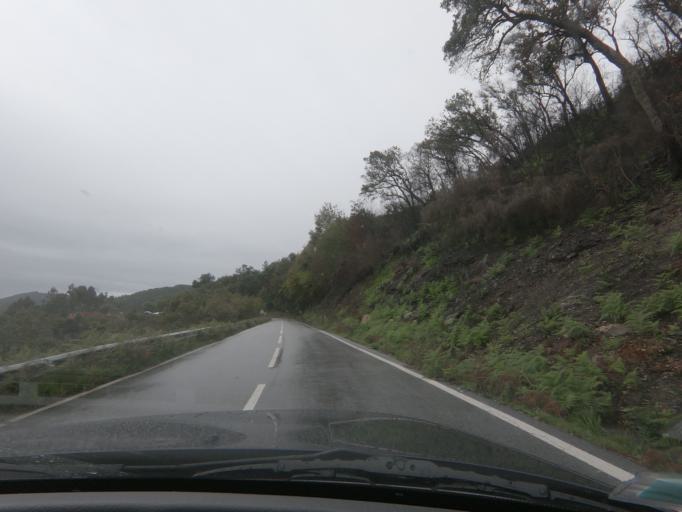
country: PT
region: Vila Real
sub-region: Mondim de Basto
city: Mondim de Basto
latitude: 41.3715
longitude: -7.9278
